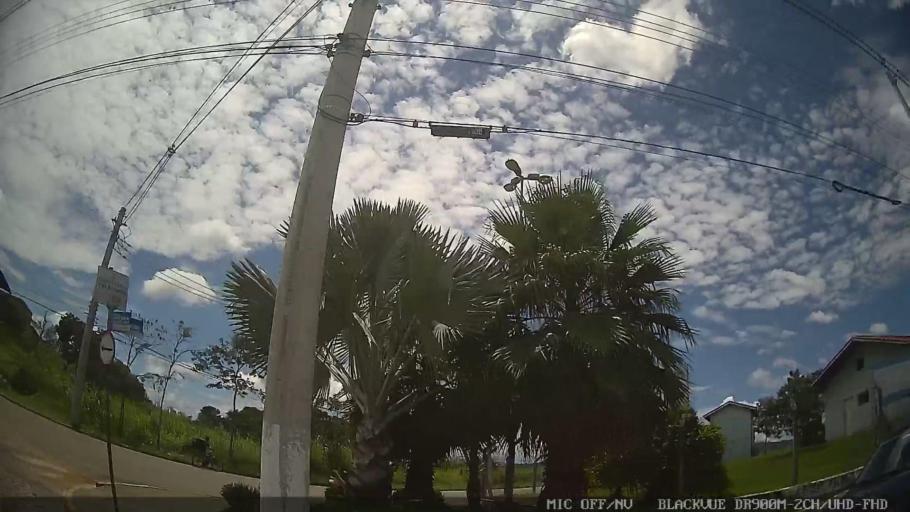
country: BR
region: Sao Paulo
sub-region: Biritiba-Mirim
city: Biritiba Mirim
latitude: -23.5805
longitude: -46.0398
